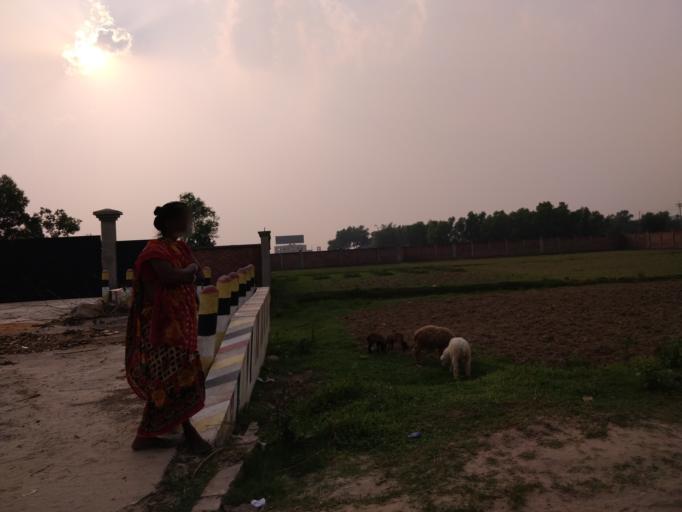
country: BD
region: Sylhet
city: Habiganj
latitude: 24.1469
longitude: 91.3514
